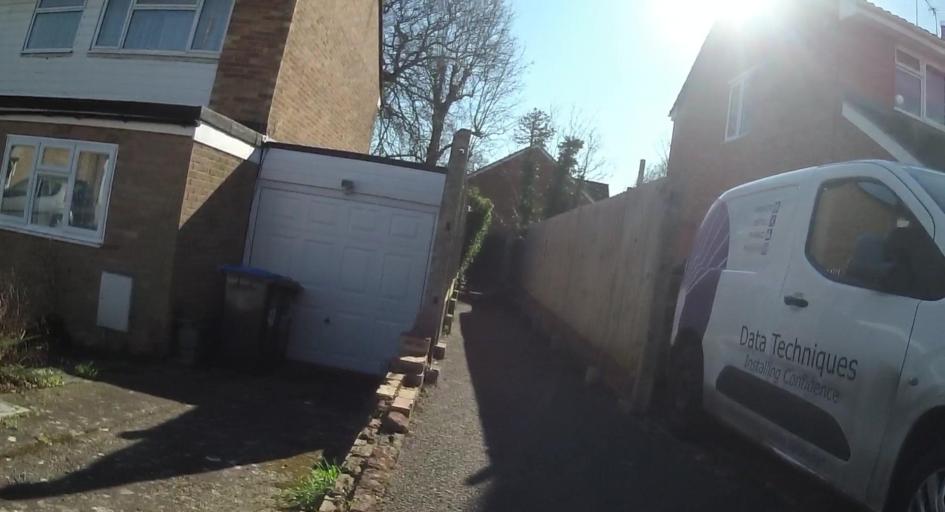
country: GB
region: England
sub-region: Surrey
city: Addlestone
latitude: 51.3633
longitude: -0.5033
